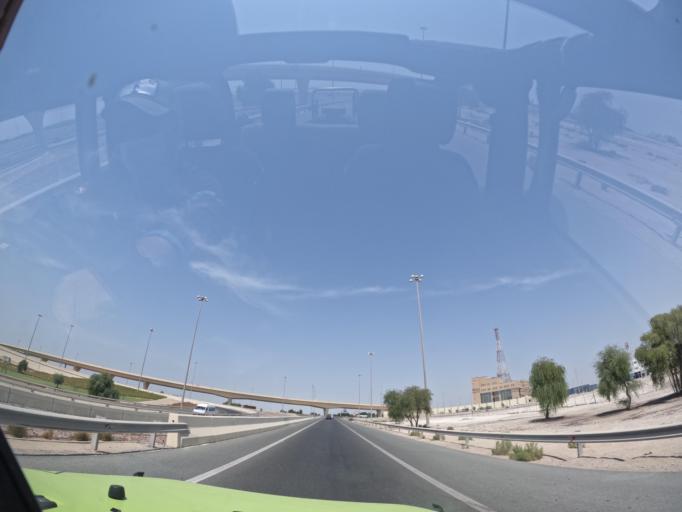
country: AE
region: Abu Dhabi
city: Abu Dhabi
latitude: 24.3091
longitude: 54.6041
